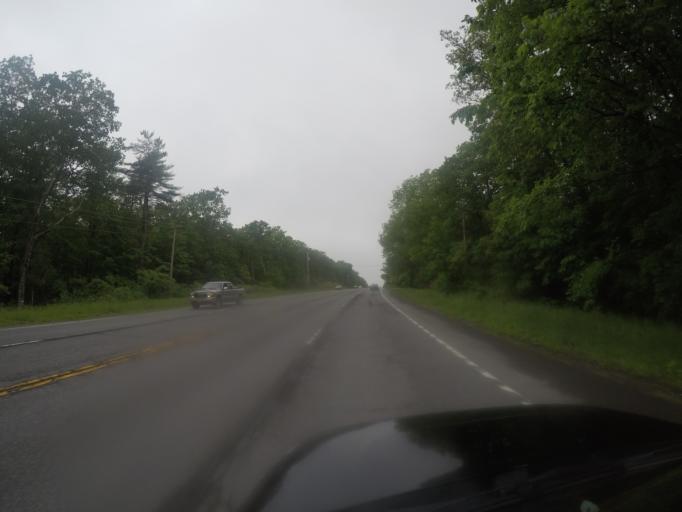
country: US
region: New York
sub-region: Ulster County
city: West Hurley
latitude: 41.9959
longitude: -74.0954
